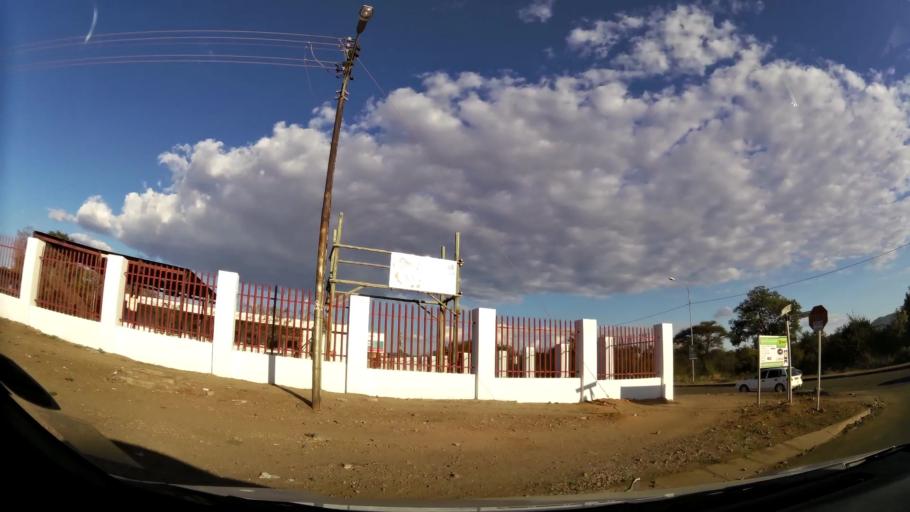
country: ZA
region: Limpopo
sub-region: Waterberg District Municipality
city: Mokopane
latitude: -24.1730
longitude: 29.0008
